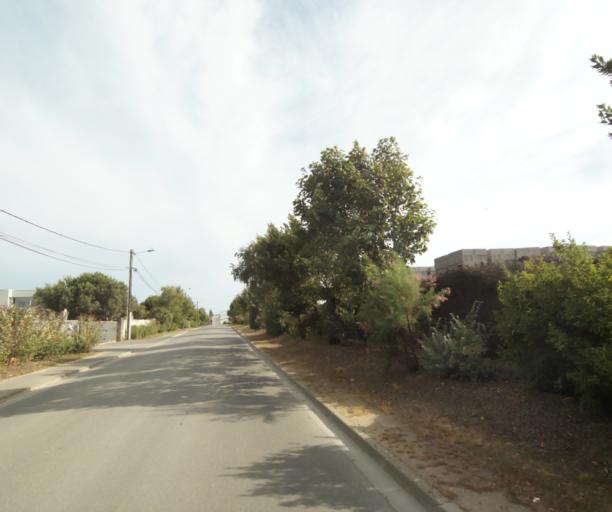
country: FR
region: Pays de la Loire
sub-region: Departement de la Vendee
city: Chateau-d'Olonne
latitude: 46.4915
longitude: -1.7298
